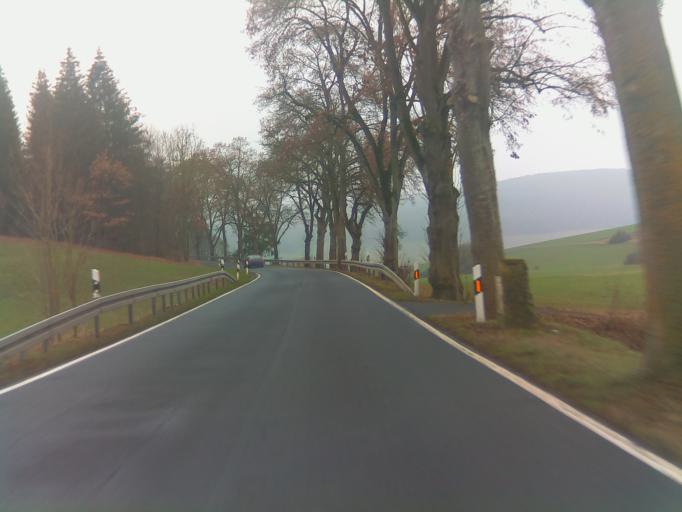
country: DE
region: Thuringia
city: Juchsen
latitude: 50.4725
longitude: 10.5448
